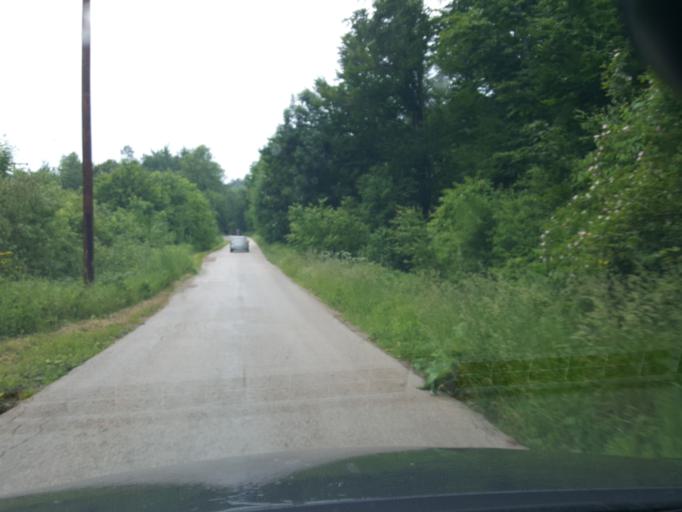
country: RS
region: Central Serbia
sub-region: Zajecarski Okrug
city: Boljevac
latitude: 43.7759
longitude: 21.9297
